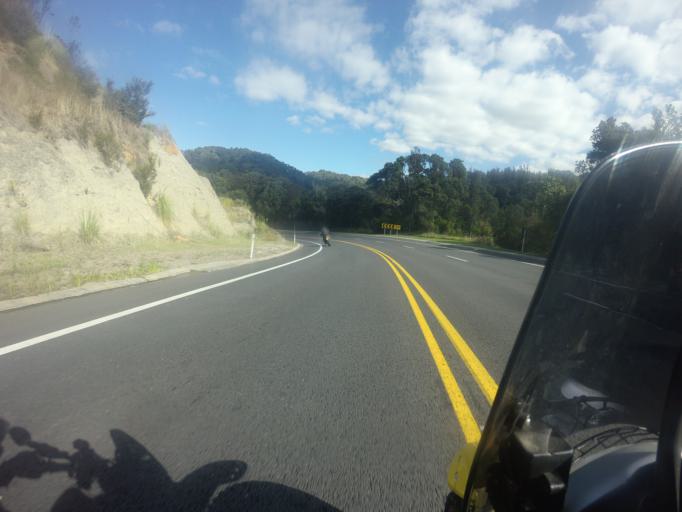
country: NZ
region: Bay of Plenty
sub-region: Whakatane District
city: Whakatane
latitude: -37.9639
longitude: 177.0281
